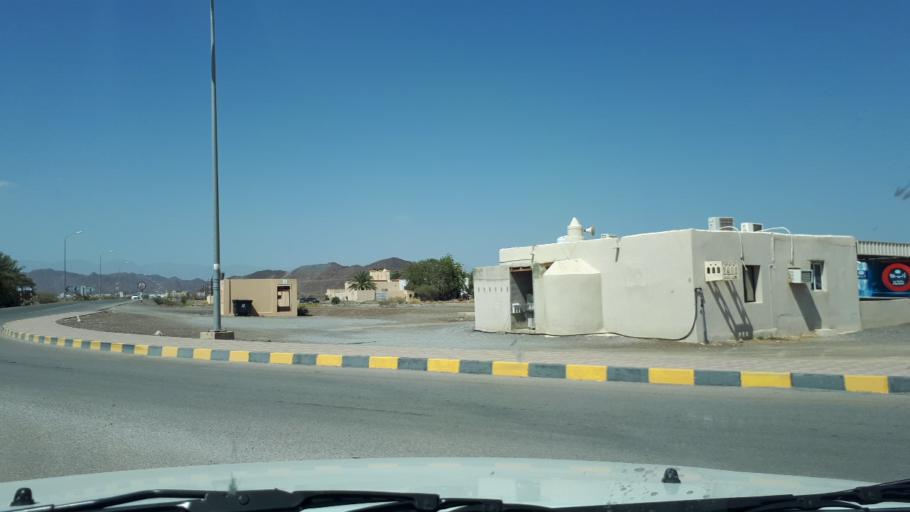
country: OM
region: Muhafazat ad Dakhiliyah
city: Bahla'
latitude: 22.9139
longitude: 57.2523
